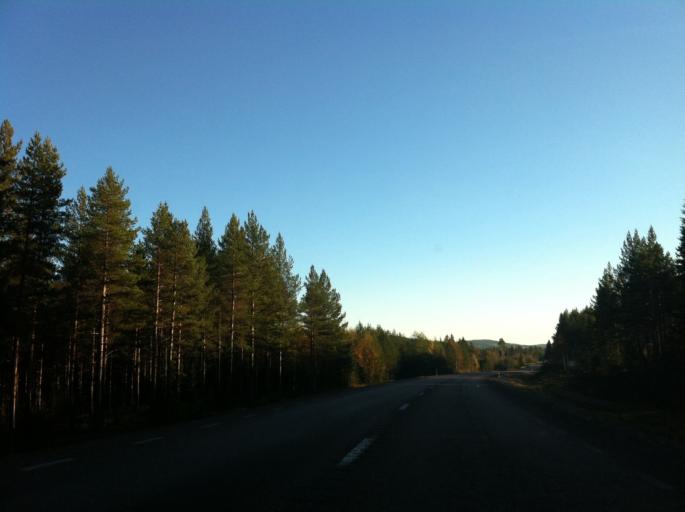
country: SE
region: Dalarna
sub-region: Rattviks Kommun
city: Raettvik
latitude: 60.8236
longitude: 15.2522
